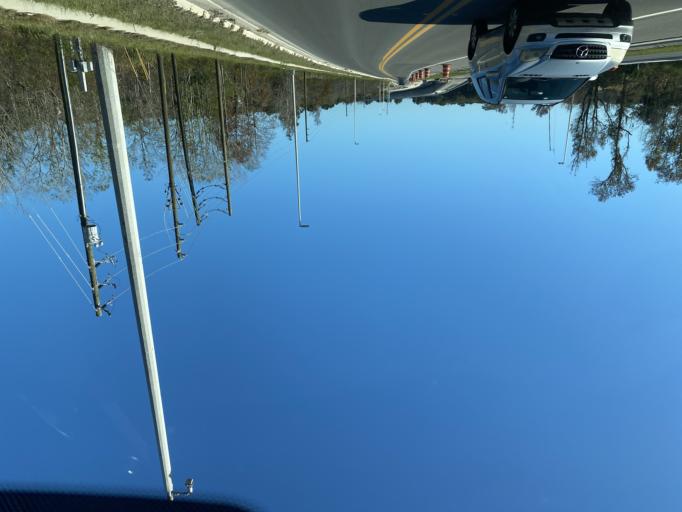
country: US
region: Florida
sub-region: Lake County
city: Mount Dora
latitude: 28.8001
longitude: -81.6170
